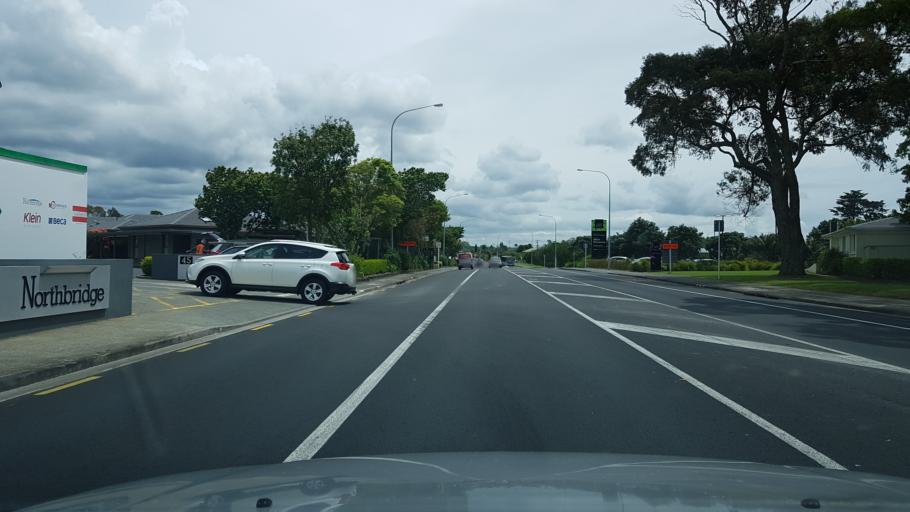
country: NZ
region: Auckland
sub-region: Auckland
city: North Shore
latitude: -36.7982
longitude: 174.7562
